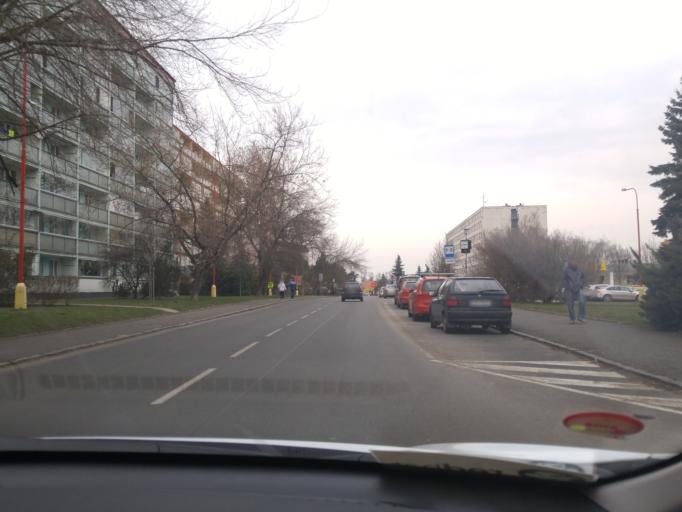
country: CZ
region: Central Bohemia
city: Neratovice
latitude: 50.2529
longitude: 14.5197
